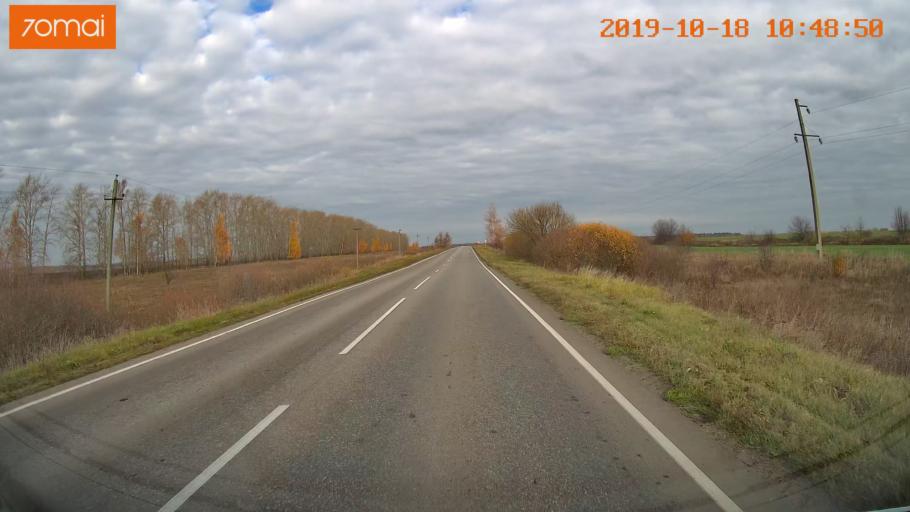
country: RU
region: Tula
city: Yepifan'
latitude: 53.7227
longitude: 38.6971
